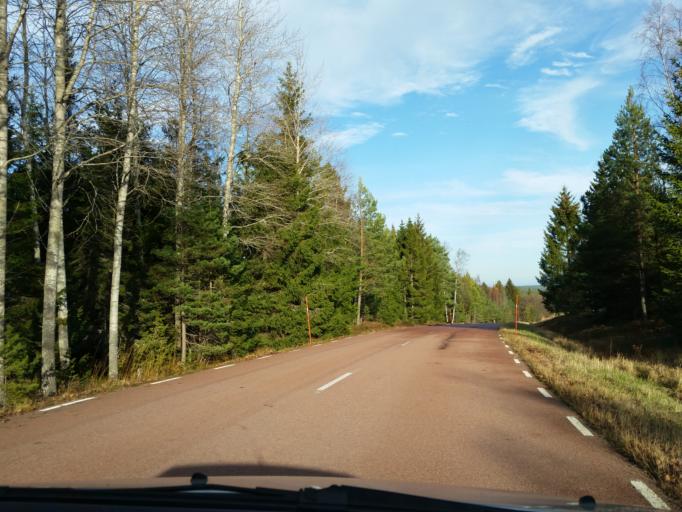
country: AX
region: Alands landsbygd
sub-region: Saltvik
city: Saltvik
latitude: 60.3403
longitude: 20.0840
